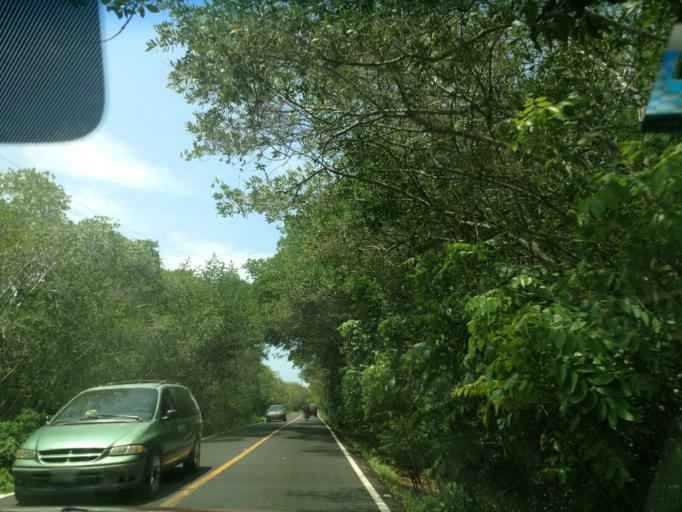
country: MX
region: Nayarit
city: San Blas
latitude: 21.5493
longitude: -105.2588
